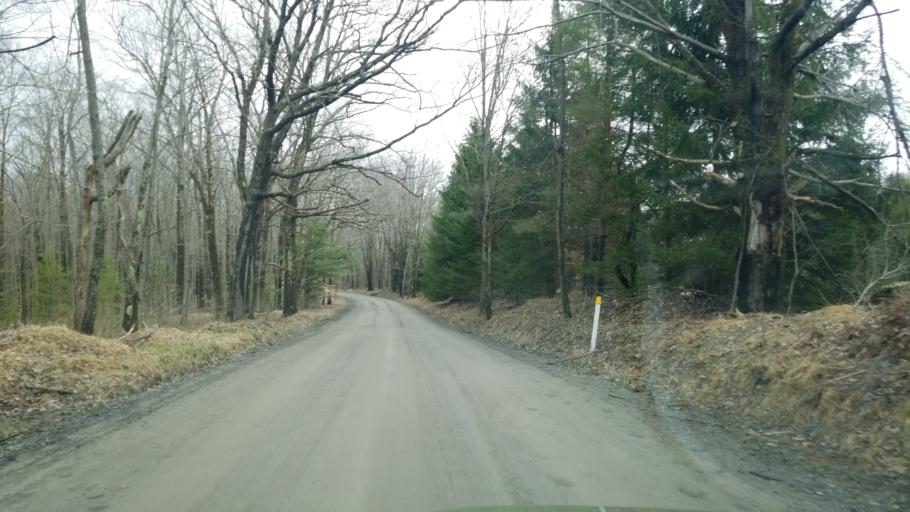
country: US
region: Pennsylvania
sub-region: Clearfield County
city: Shiloh
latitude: 41.1786
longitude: -78.3459
